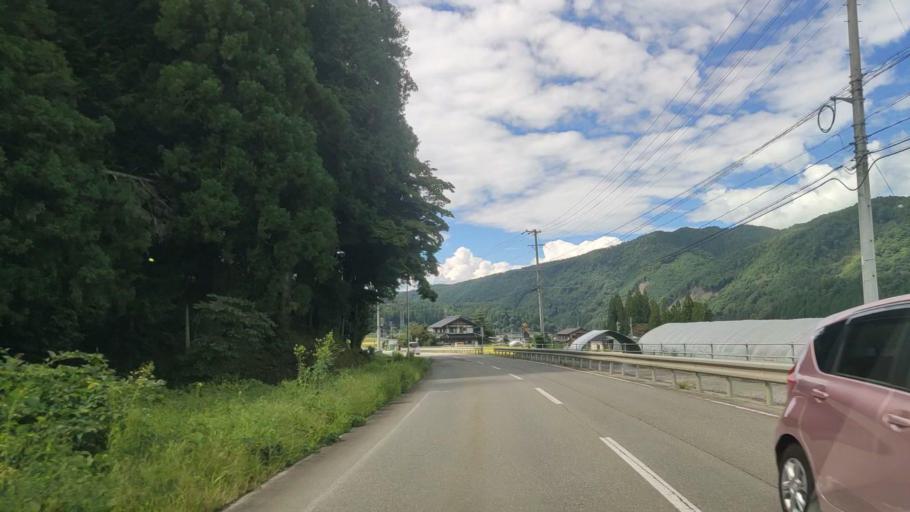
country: JP
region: Gifu
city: Takayama
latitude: 36.1740
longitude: 137.2919
